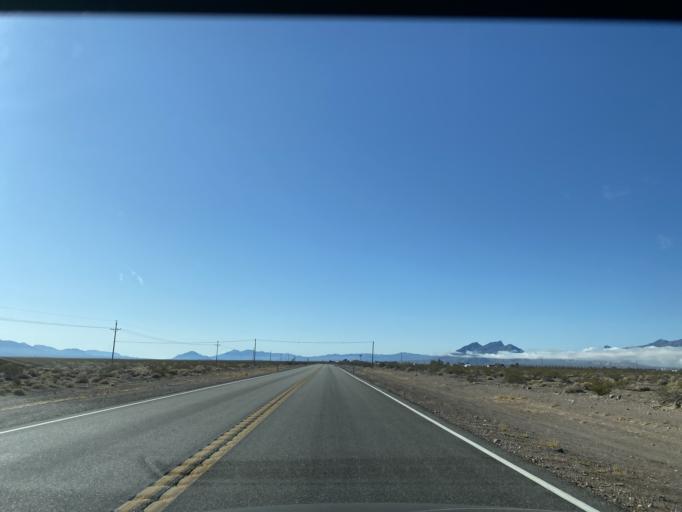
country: US
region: Nevada
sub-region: Nye County
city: Beatty
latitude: 36.5125
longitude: -116.4204
